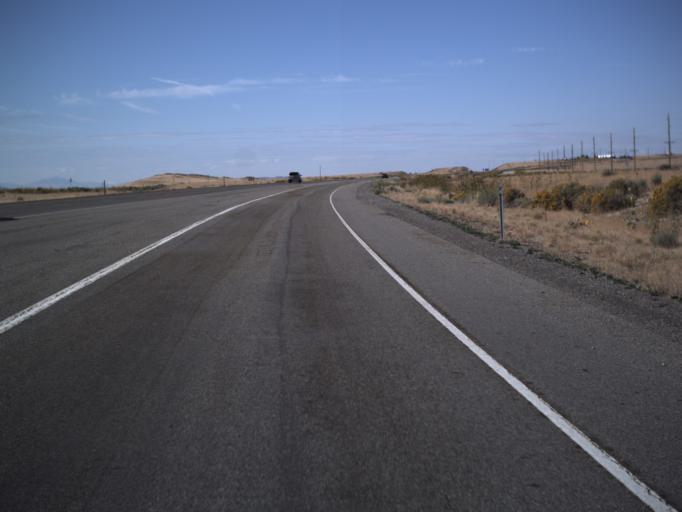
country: US
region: Utah
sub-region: Tooele County
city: Grantsville
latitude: 40.7673
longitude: -112.9885
